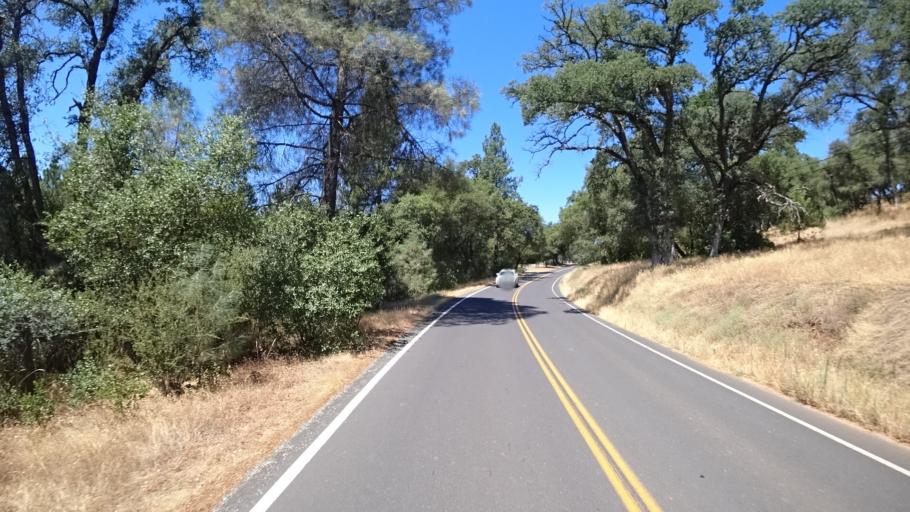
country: US
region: California
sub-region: Calaveras County
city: Murphys
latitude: 38.1314
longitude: -120.4484
